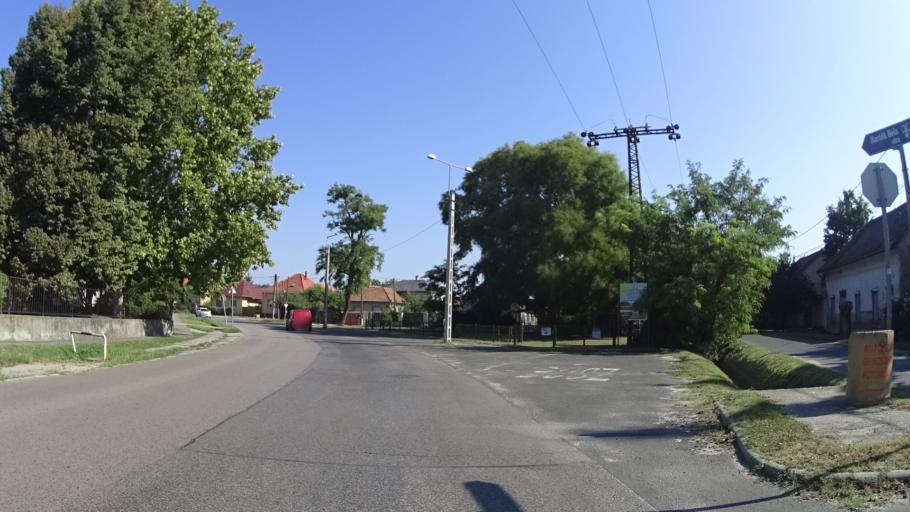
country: HU
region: Pest
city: Dunakeszi
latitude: 47.6321
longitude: 19.1327
